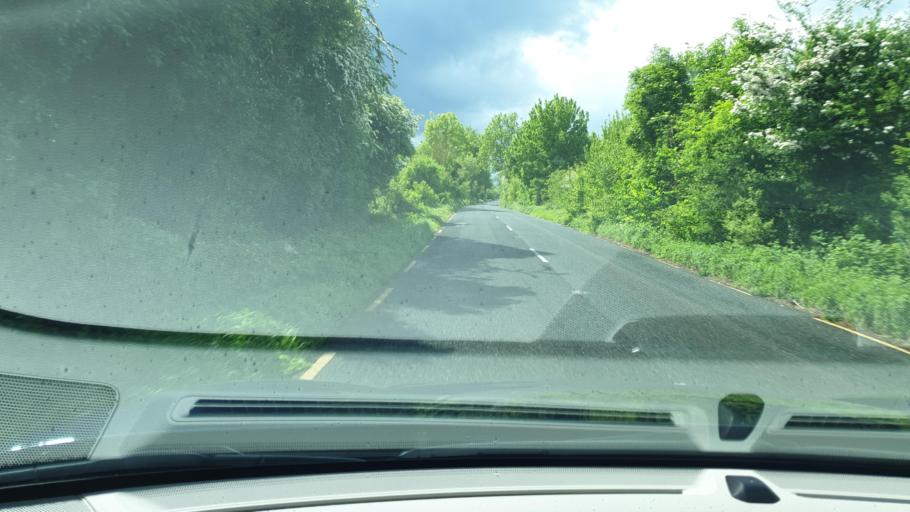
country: IE
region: Leinster
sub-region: Uibh Fhaili
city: Clara
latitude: 53.2367
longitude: -7.6659
